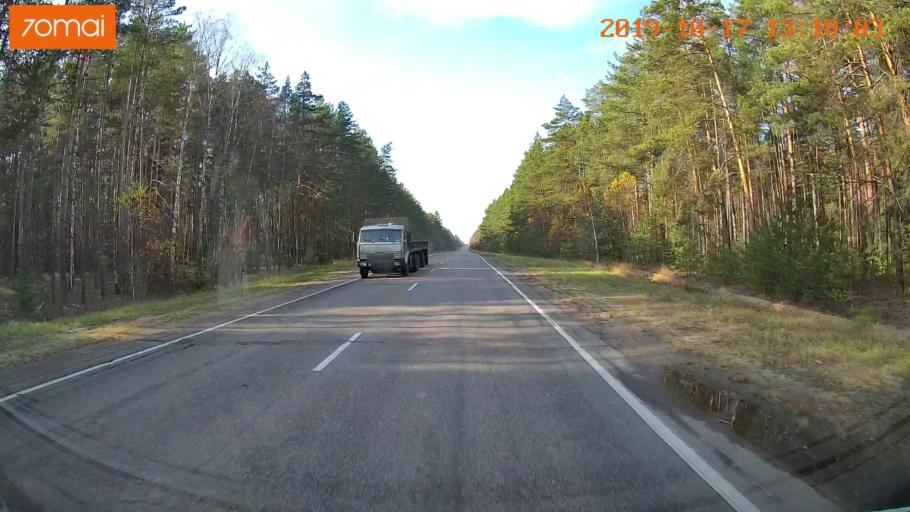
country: RU
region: Rjazan
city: Gus'-Zheleznyy
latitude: 55.0606
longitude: 41.1067
